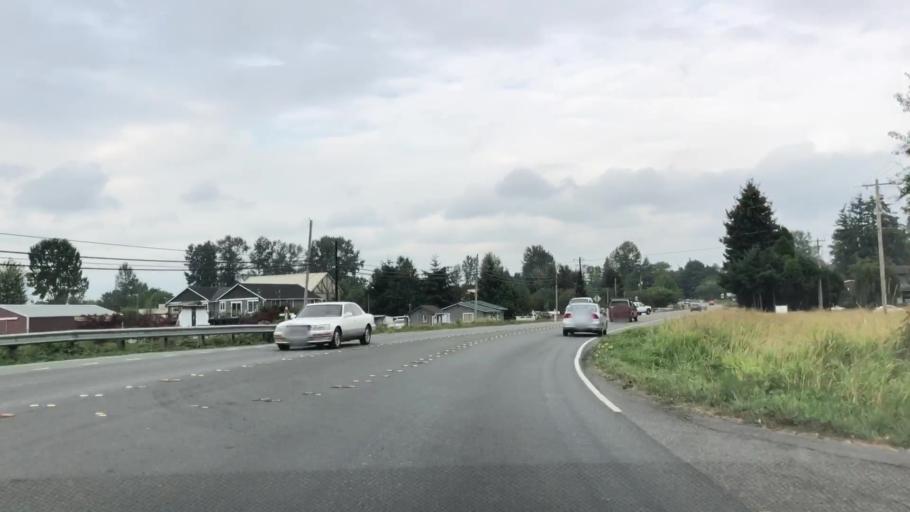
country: US
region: Washington
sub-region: Snohomish County
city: Snohomish
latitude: 47.9133
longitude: -122.0768
